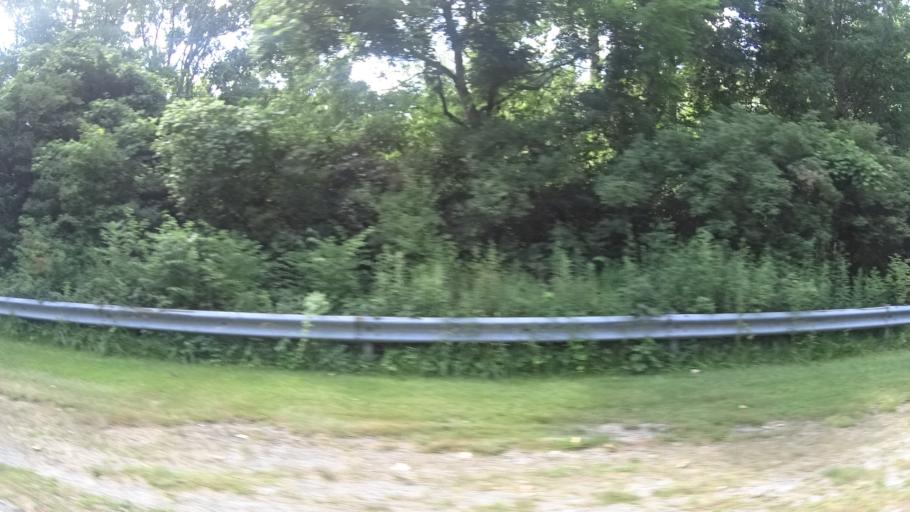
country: US
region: Ohio
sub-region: Erie County
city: Sandusky
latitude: 41.4243
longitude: -82.6648
